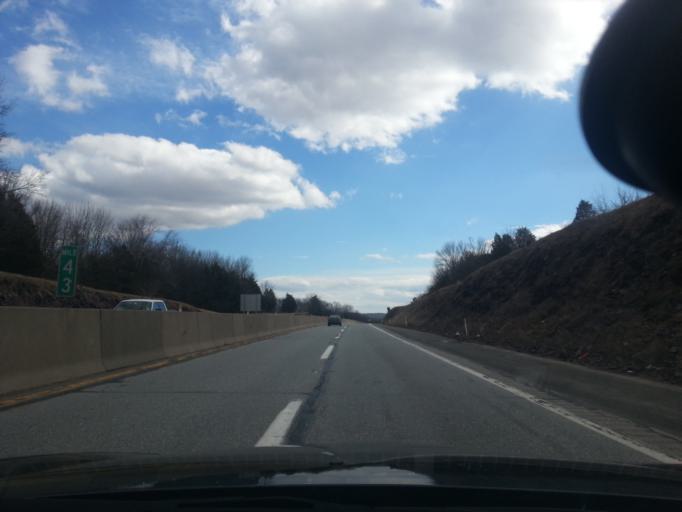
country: US
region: Pennsylvania
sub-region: Bucks County
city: Spinnerstown
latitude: 40.4267
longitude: -75.4180
